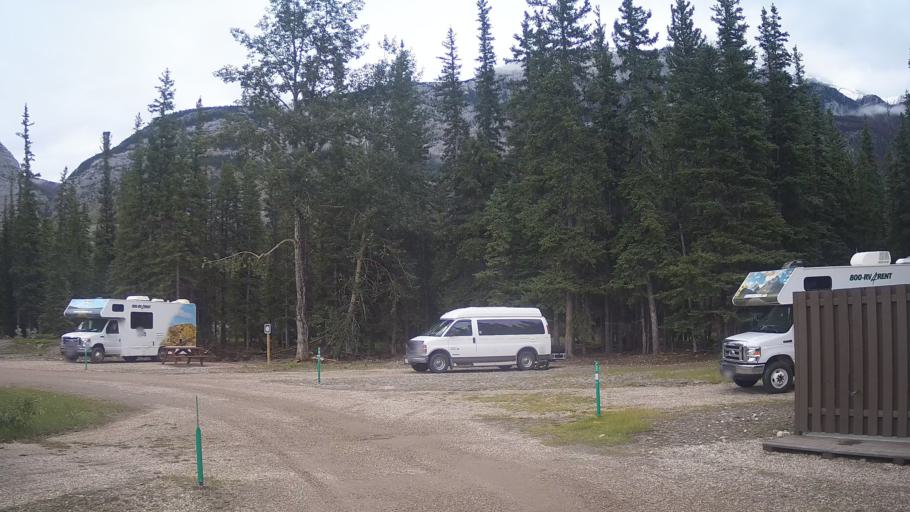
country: CA
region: Alberta
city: Jasper Park Lodge
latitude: 53.0151
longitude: -118.0821
